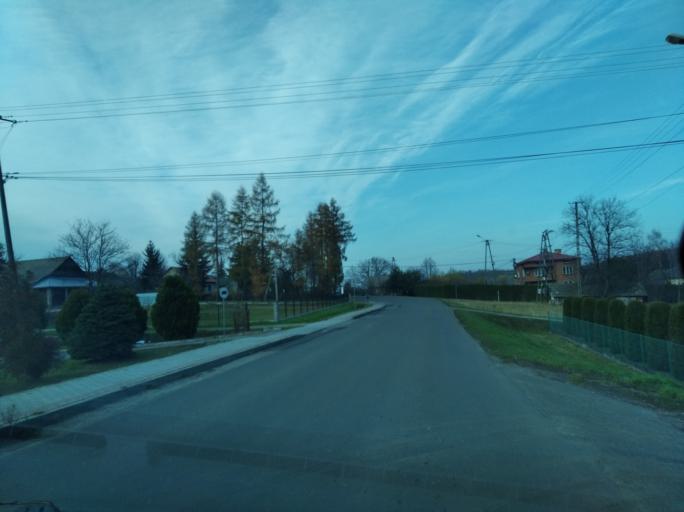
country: PL
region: Subcarpathian Voivodeship
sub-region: Powiat ropczycko-sedziszowski
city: Iwierzyce
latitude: 50.0294
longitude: 21.7554
